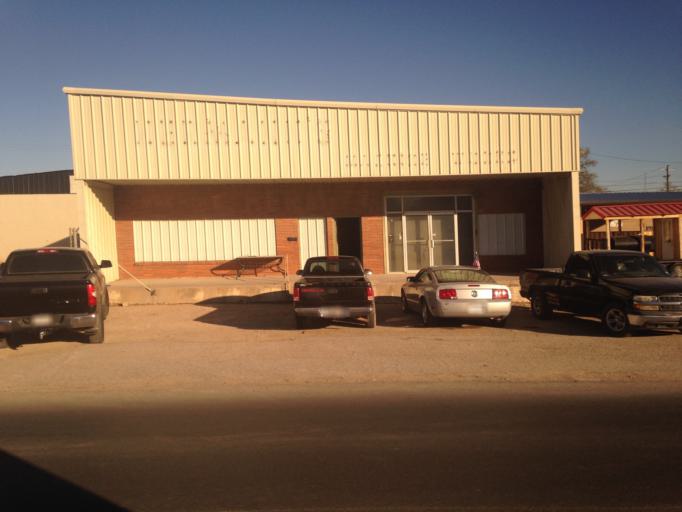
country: US
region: Texas
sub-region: Taylor County
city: Abilene
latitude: 32.4535
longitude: -99.7263
